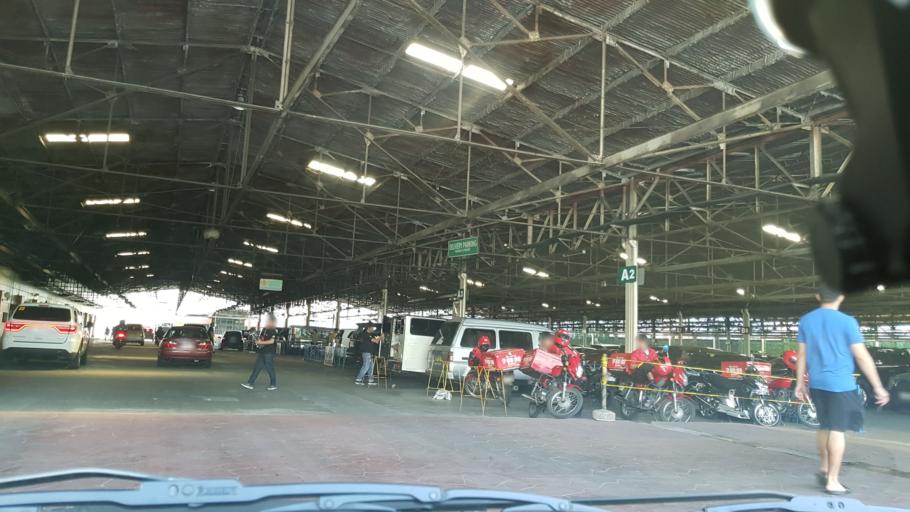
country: PH
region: Metro Manila
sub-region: Marikina
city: Calumpang
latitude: 14.6310
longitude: 121.0814
